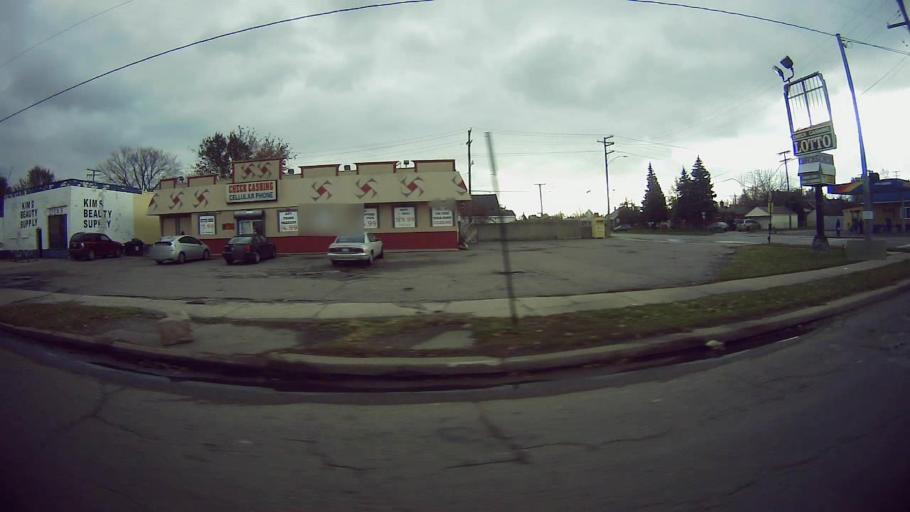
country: US
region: Michigan
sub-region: Wayne County
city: Hamtramck
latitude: 42.4205
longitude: -83.0027
